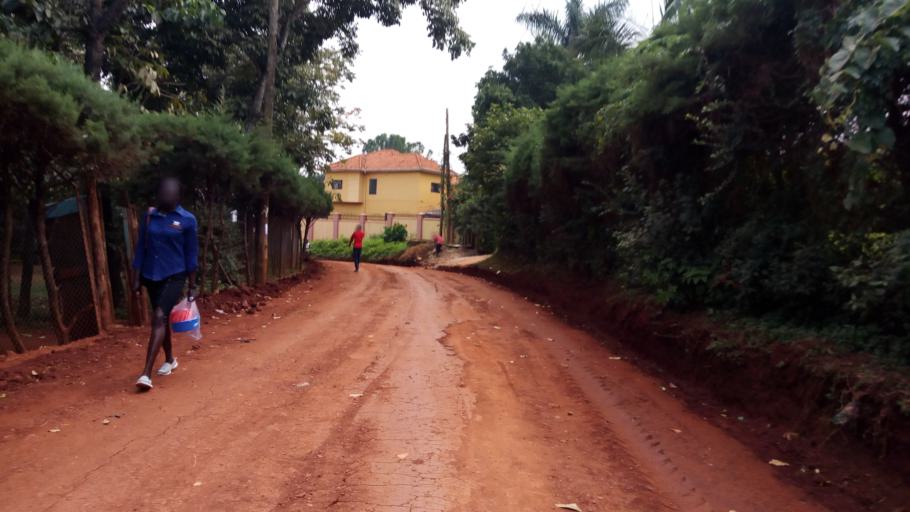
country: UG
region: Central Region
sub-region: Wakiso District
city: Kireka
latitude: 0.3213
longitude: 32.6316
